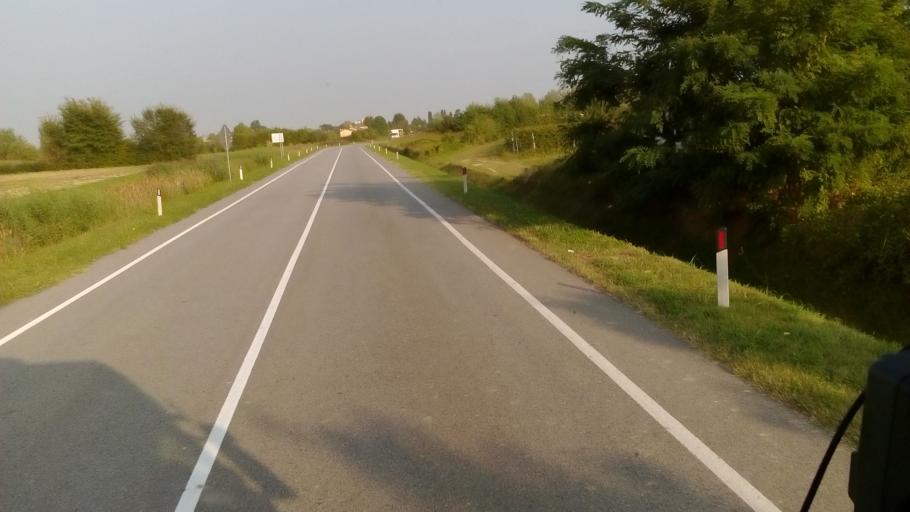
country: IT
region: Veneto
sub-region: Provincia di Padova
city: Mejaniga
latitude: 45.4721
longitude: 11.9065
